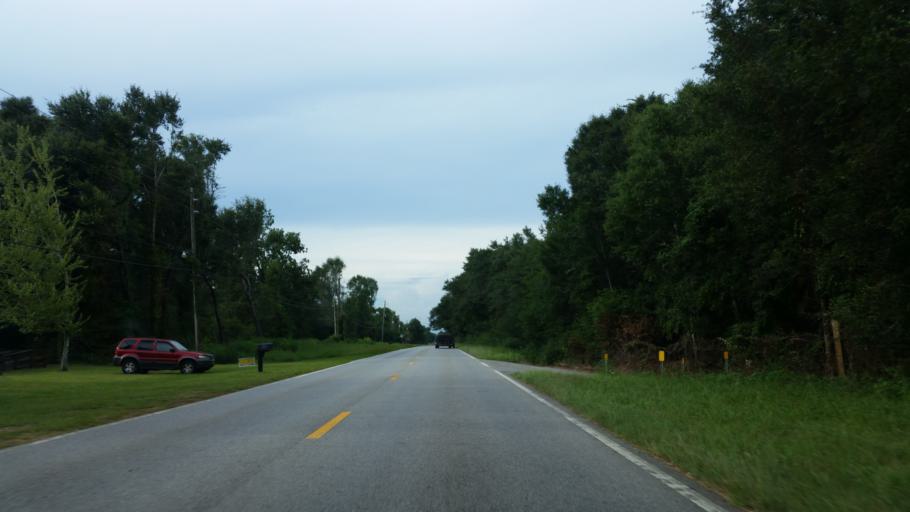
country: US
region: Florida
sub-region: Santa Rosa County
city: Pace
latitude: 30.5935
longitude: -87.1113
